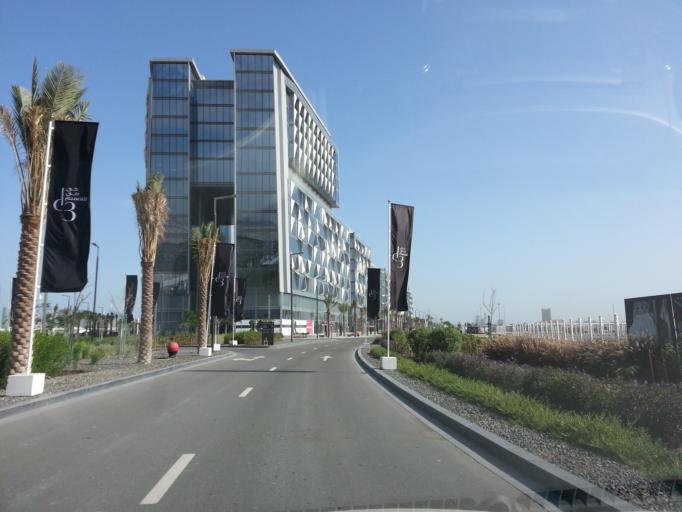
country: AE
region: Dubai
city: Dubai
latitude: 25.1854
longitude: 55.2971
